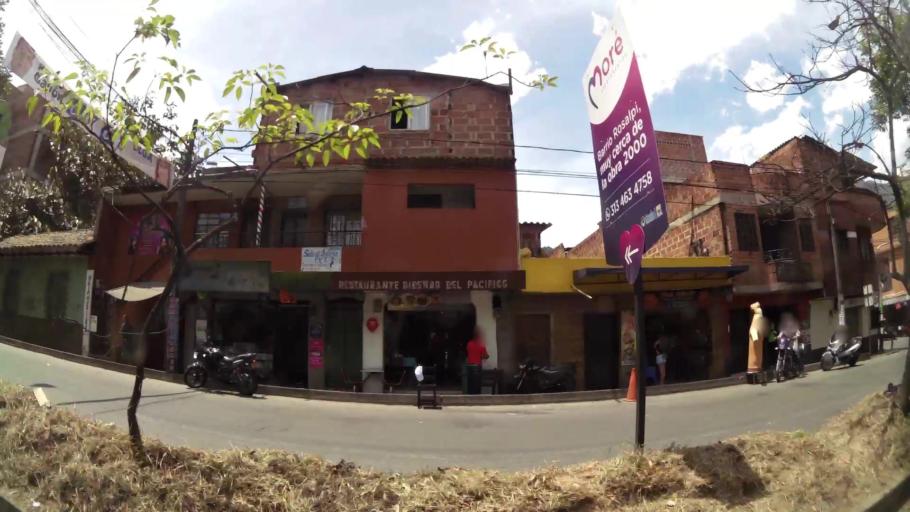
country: CO
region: Antioquia
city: Bello
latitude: 6.3406
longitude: -75.5641
